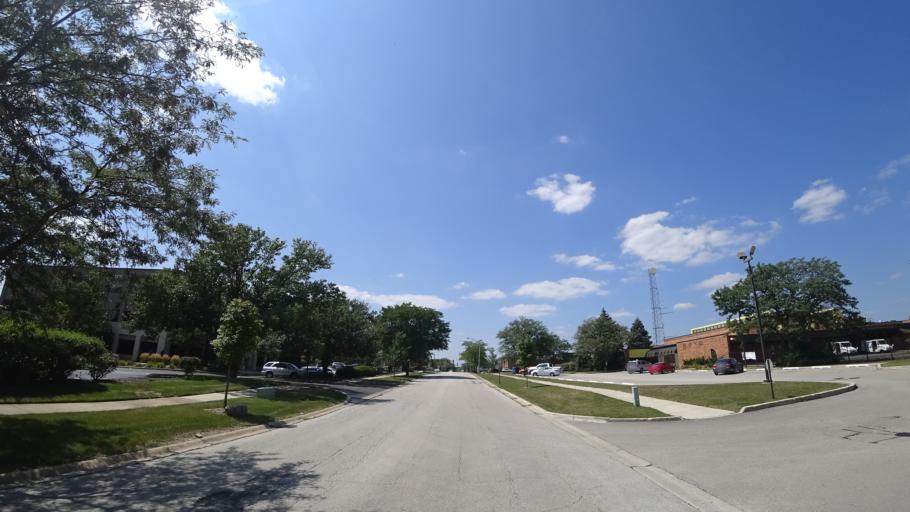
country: US
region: Illinois
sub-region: Cook County
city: Orland Park
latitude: 41.6278
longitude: -87.8509
